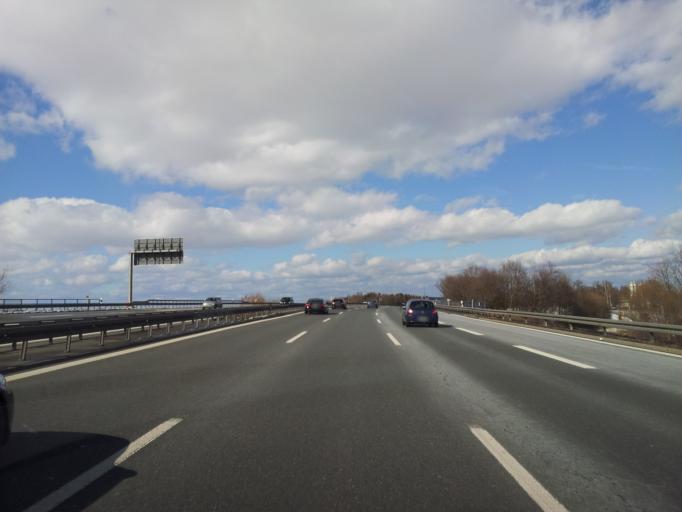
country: DE
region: Bavaria
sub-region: Upper Franconia
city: Munchberg
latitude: 50.1700
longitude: 11.7461
